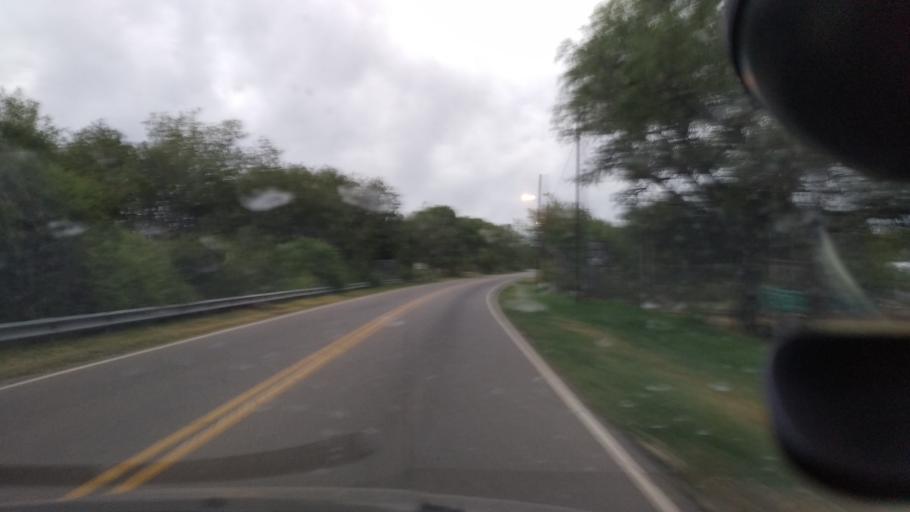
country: AR
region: Cordoba
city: Villa Las Rosas
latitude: -31.9256
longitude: -65.0396
